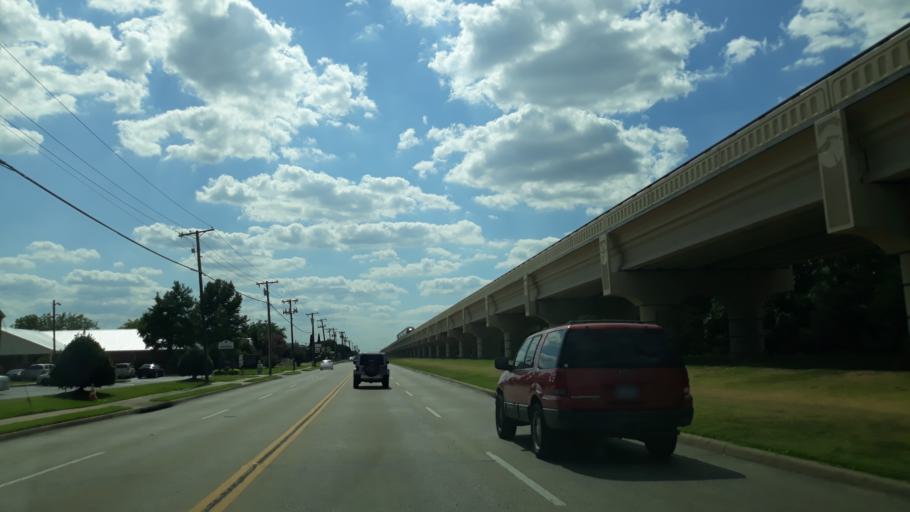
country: US
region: Texas
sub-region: Dallas County
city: Irving
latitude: 32.8155
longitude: -96.9821
